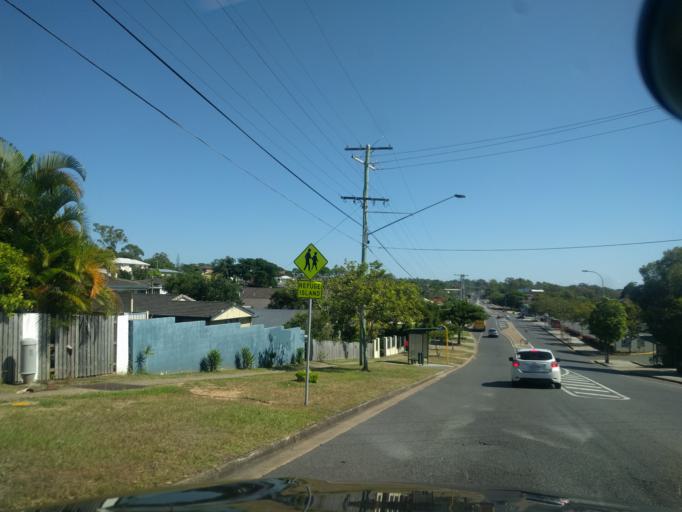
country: AU
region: Queensland
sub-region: Brisbane
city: Stafford Heights
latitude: -27.3936
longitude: 153.0109
